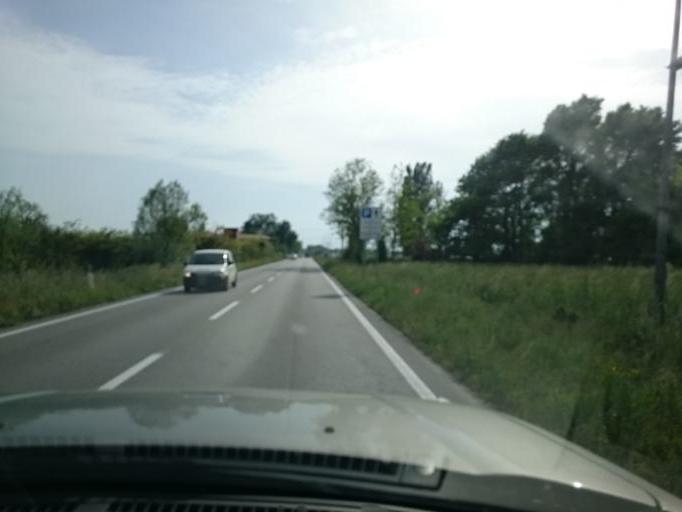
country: IT
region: Veneto
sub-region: Provincia di Venezia
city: Tessera
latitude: 45.4979
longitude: 12.3176
